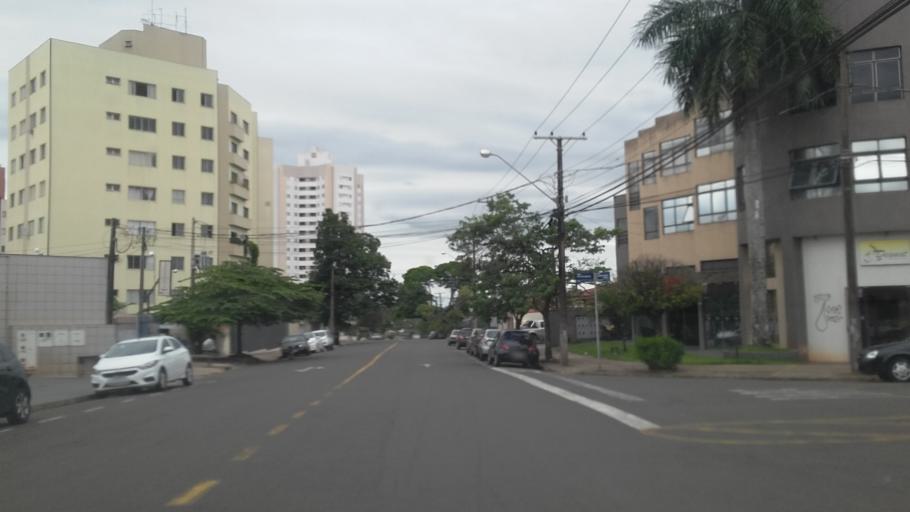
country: BR
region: Parana
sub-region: Londrina
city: Londrina
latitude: -23.3042
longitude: -51.1791
